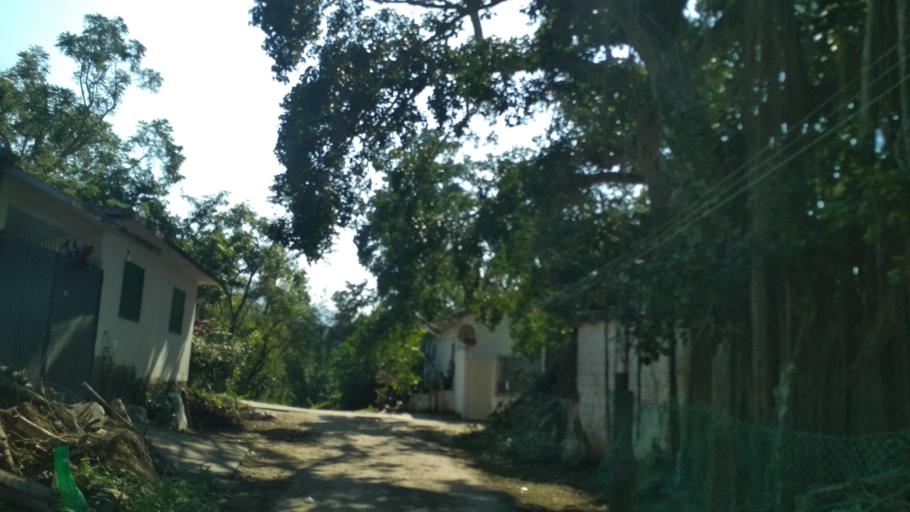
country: MX
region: Veracruz
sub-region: Papantla
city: Polutla
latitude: 20.4623
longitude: -97.1934
